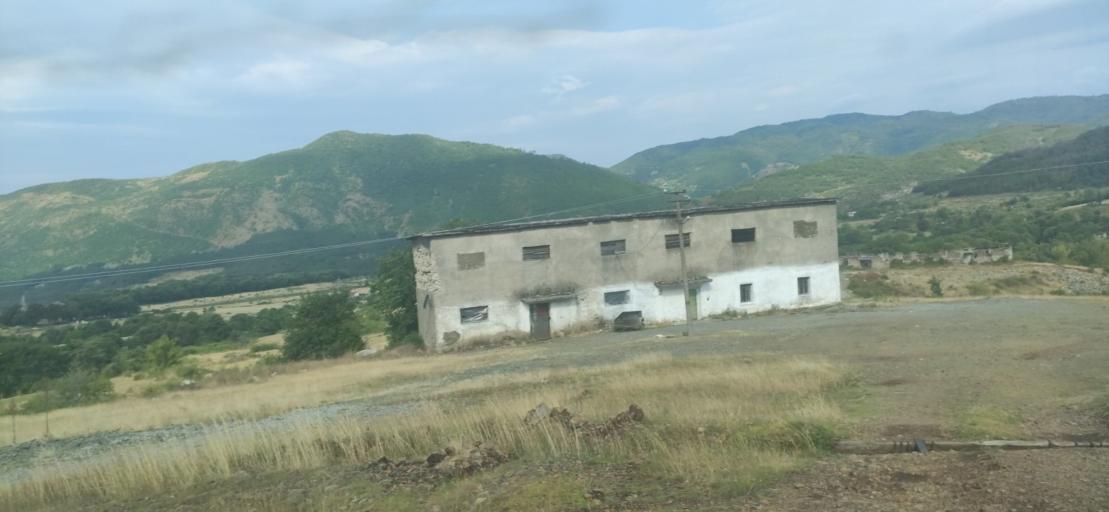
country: AL
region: Shkoder
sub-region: Rrethi i Pukes
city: Iballe
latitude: 42.1876
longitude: 20.0036
